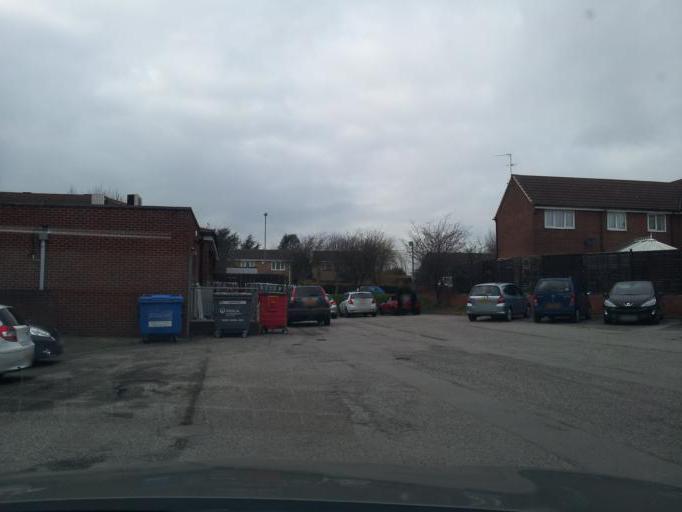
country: GB
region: England
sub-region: Lincolnshire
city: Great Gonerby
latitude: 52.9143
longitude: -0.6655
